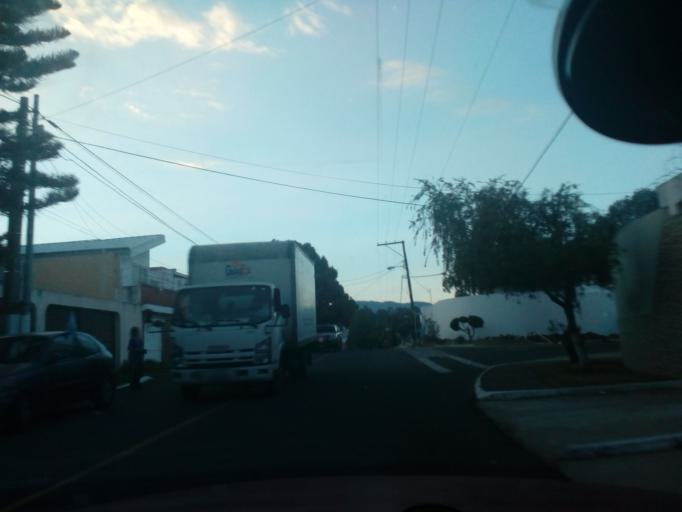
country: GT
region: Guatemala
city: Mixco
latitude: 14.6033
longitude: -90.5786
